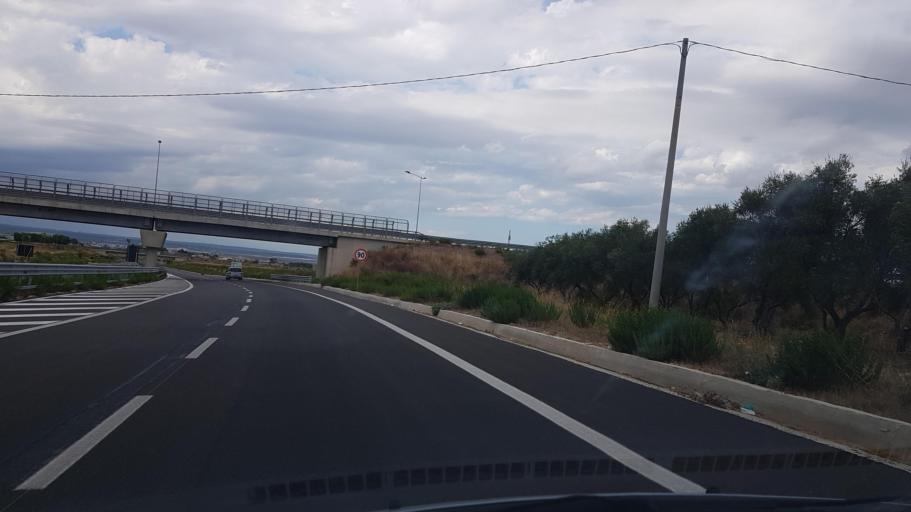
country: IT
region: Apulia
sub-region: Provincia di Taranto
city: Taranto
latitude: 40.4503
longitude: 17.2848
